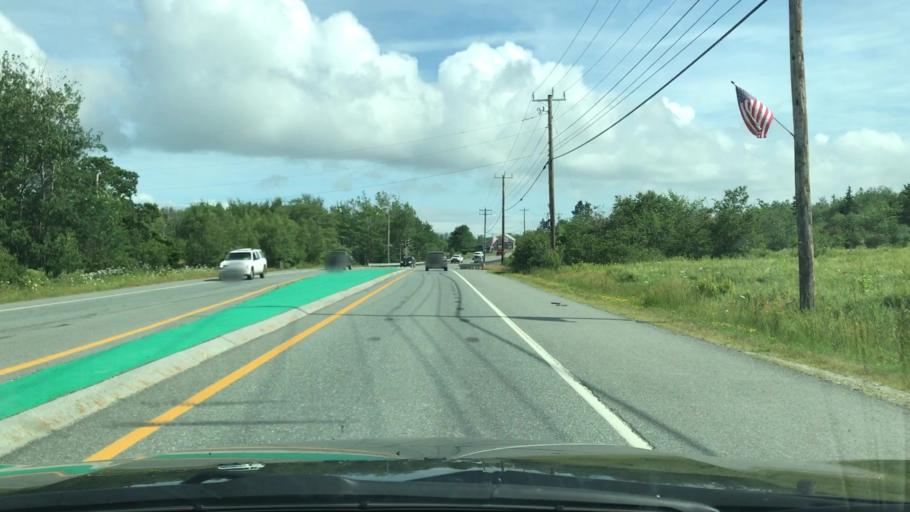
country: US
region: Maine
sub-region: Hancock County
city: Trenton
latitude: 44.4698
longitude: -68.3636
